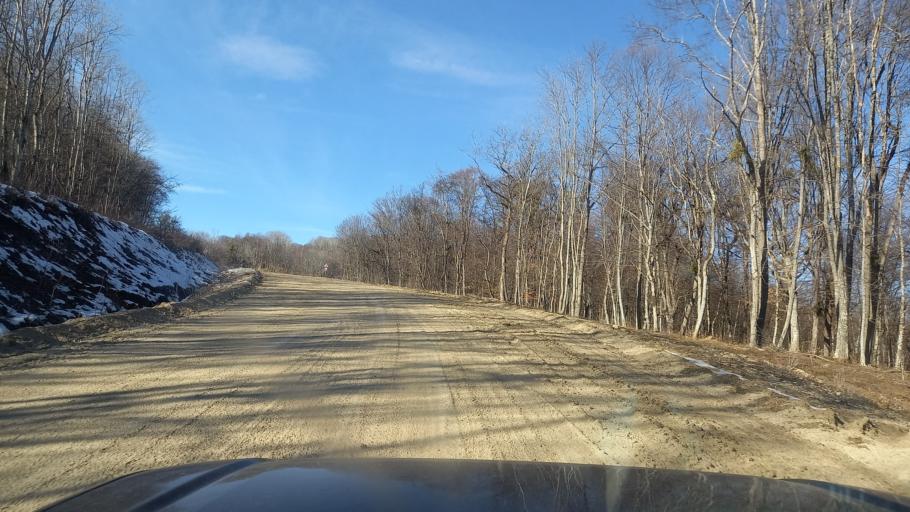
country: RU
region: Adygeya
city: Kamennomostskiy
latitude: 44.2811
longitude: 40.3243
